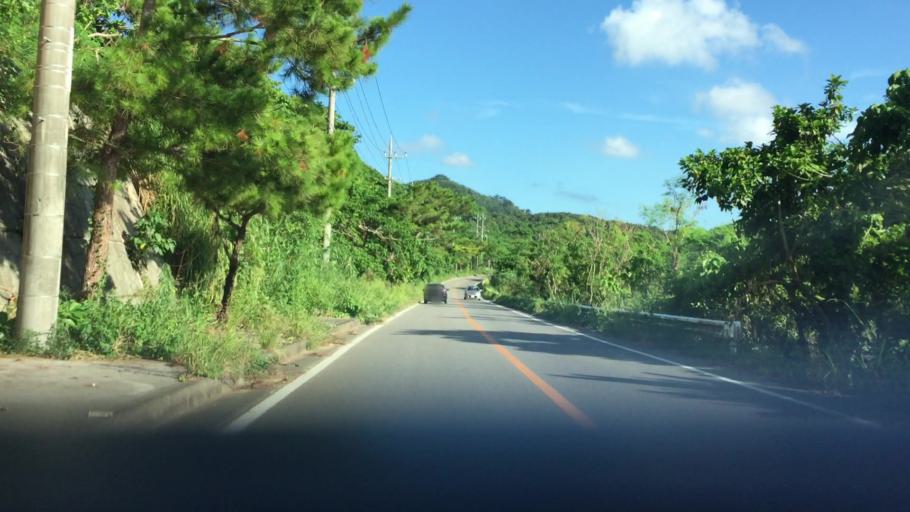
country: JP
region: Okinawa
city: Ishigaki
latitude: 24.3845
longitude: 124.1524
